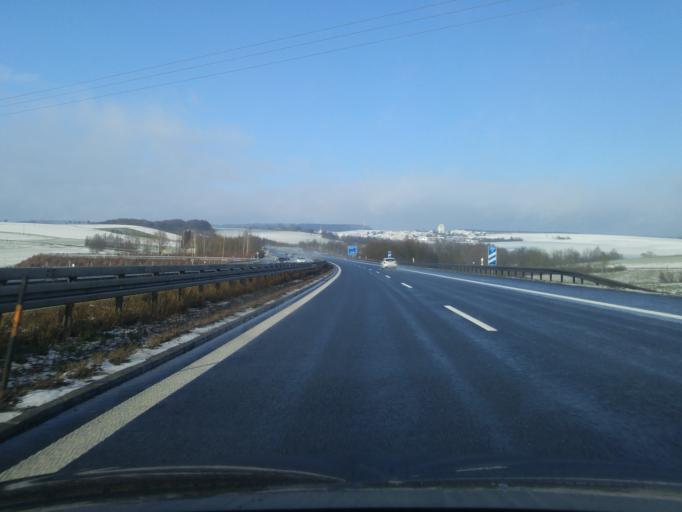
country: DE
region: Bavaria
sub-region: Regierungsbezirk Unterfranken
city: Wasserlosen
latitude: 50.0618
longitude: 10.0497
